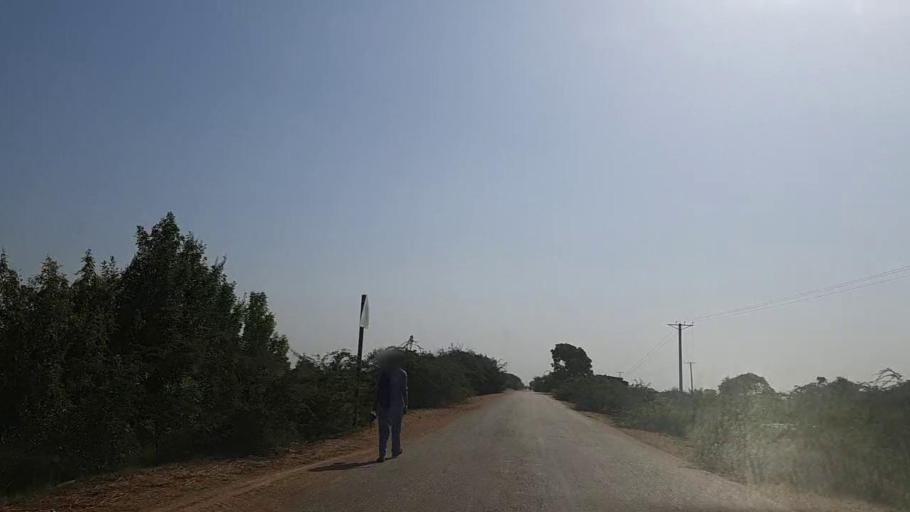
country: PK
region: Sindh
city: Mirpur Batoro
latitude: 24.5987
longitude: 68.2940
